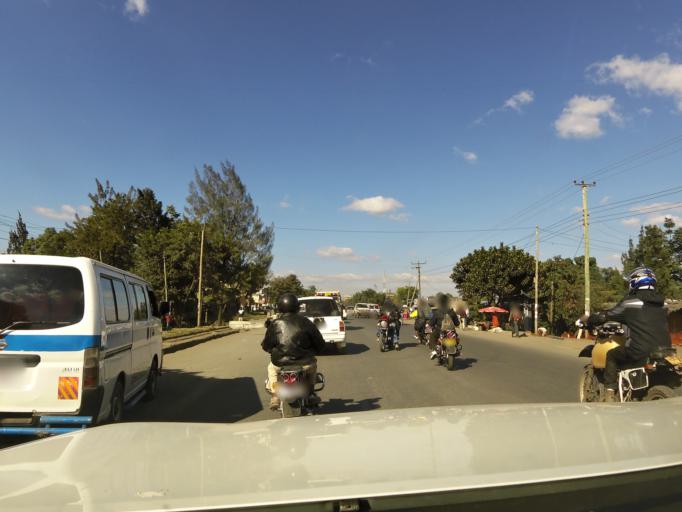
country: TZ
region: Arusha
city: Arusha
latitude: -3.3756
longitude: 36.6717
